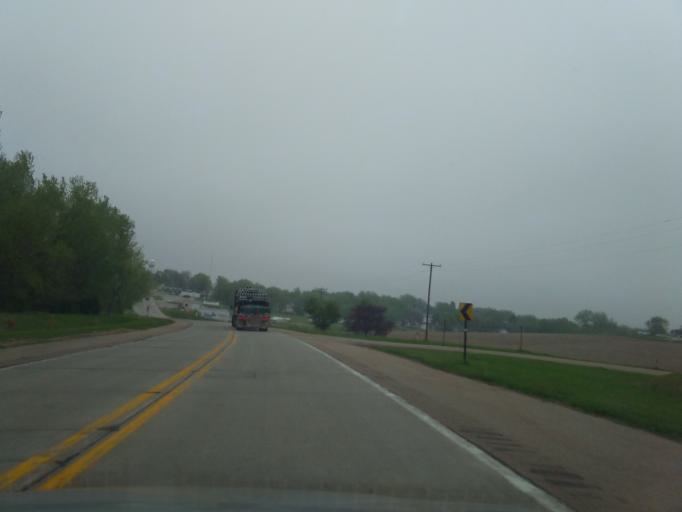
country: US
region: Nebraska
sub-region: Burt County
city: Oakland
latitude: 41.8284
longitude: -96.4627
